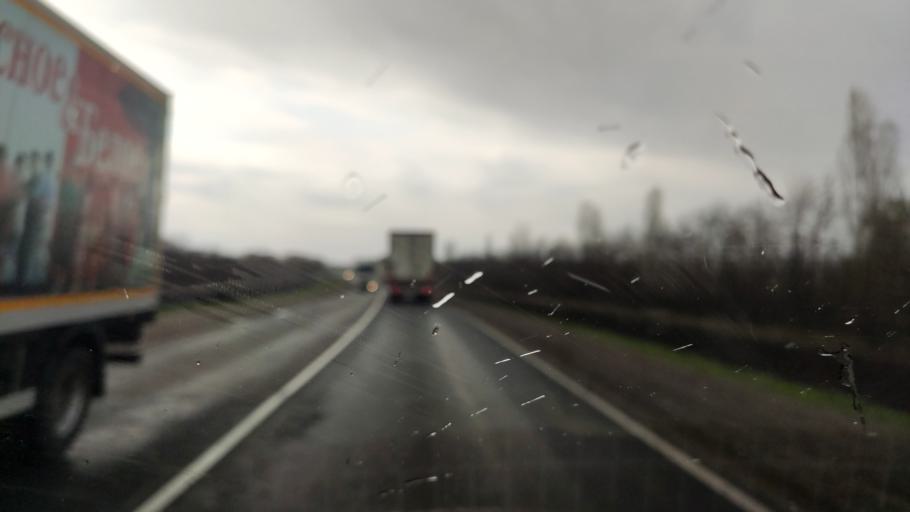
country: RU
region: Voronezj
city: Nizhnedevitsk
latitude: 51.5737
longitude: 38.3285
